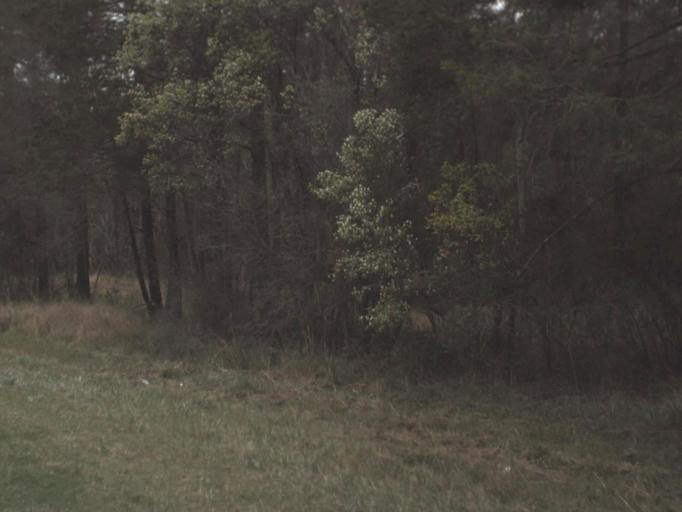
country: US
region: Florida
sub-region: Gulf County
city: Wewahitchka
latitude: 30.1517
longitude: -84.9685
